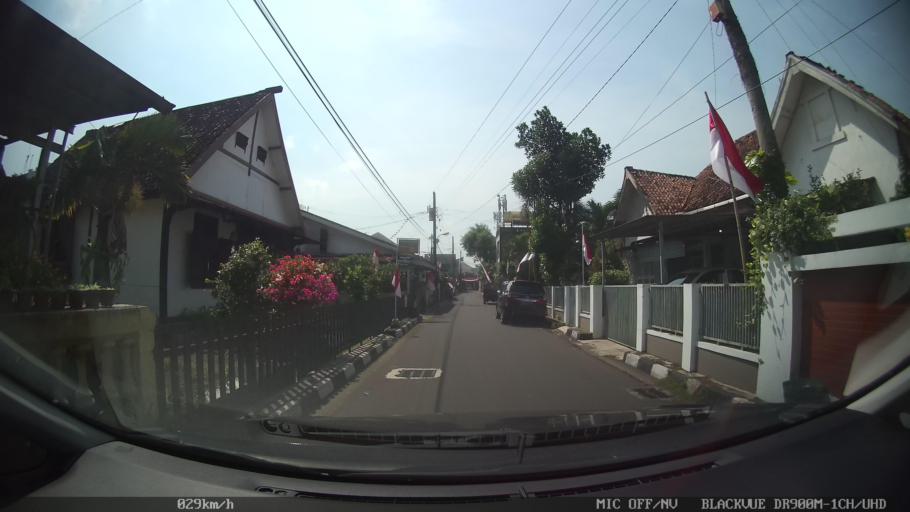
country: ID
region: Daerah Istimewa Yogyakarta
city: Yogyakarta
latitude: -7.7841
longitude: 110.3650
